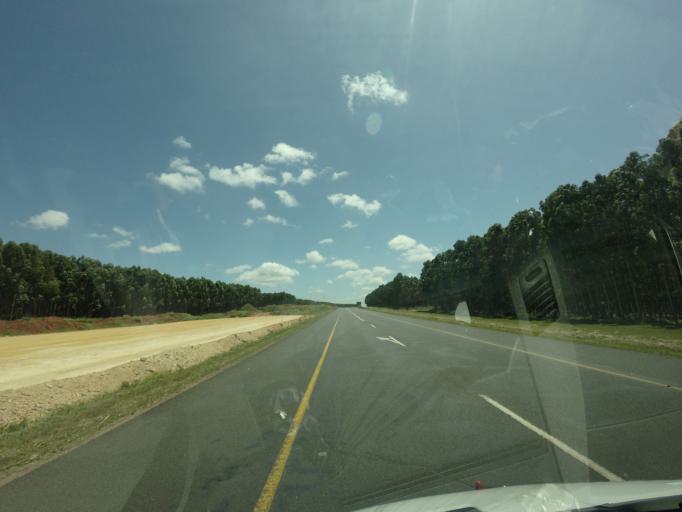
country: ZA
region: KwaZulu-Natal
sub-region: uThungulu District Municipality
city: Empangeni
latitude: -28.7412
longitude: 31.9390
